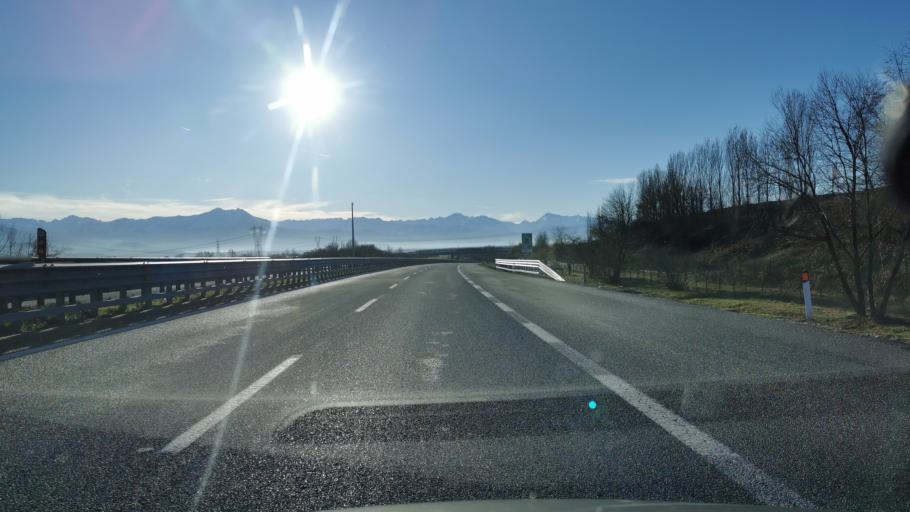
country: IT
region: Piedmont
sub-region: Provincia di Cuneo
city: Magliano Alpi
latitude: 44.4731
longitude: 7.7878
